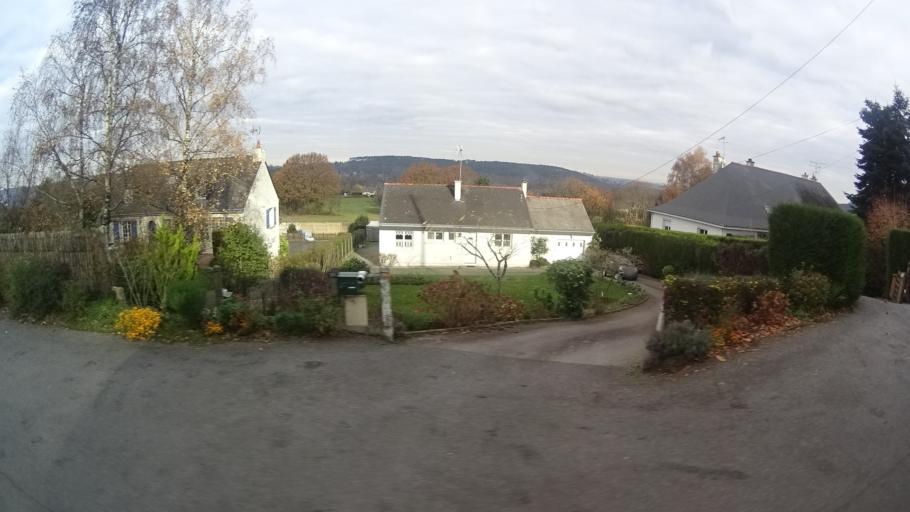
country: FR
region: Pays de la Loire
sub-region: Departement de la Loire-Atlantique
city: Saint-Nicolas-de-Redon
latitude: 47.6460
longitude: -2.0559
